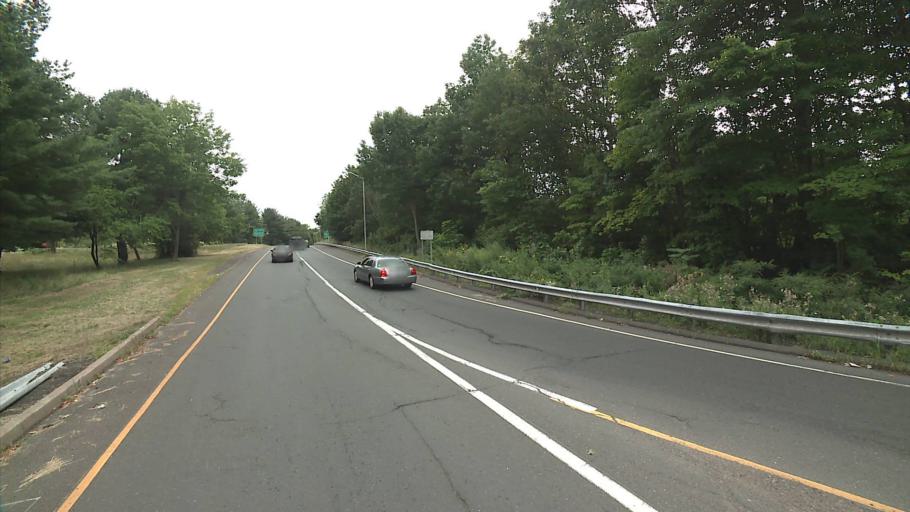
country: US
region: Connecticut
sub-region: Hartford County
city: West Hartford
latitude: 41.7541
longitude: -72.7371
